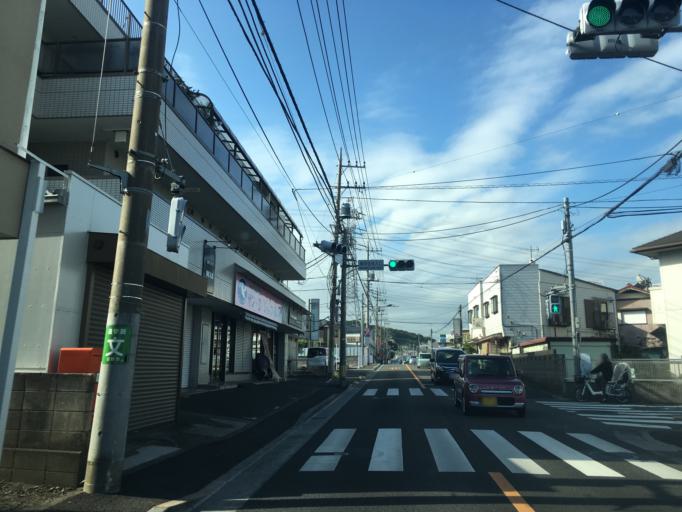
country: JP
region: Tokyo
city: Hino
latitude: 35.6512
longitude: 139.3903
